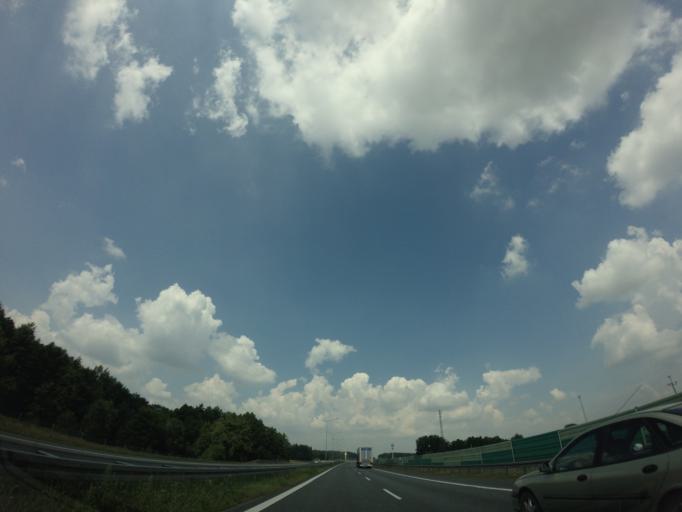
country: PL
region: Silesian Voivodeship
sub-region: Powiat gliwicki
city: Sosnicowice
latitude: 50.3043
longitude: 18.5533
